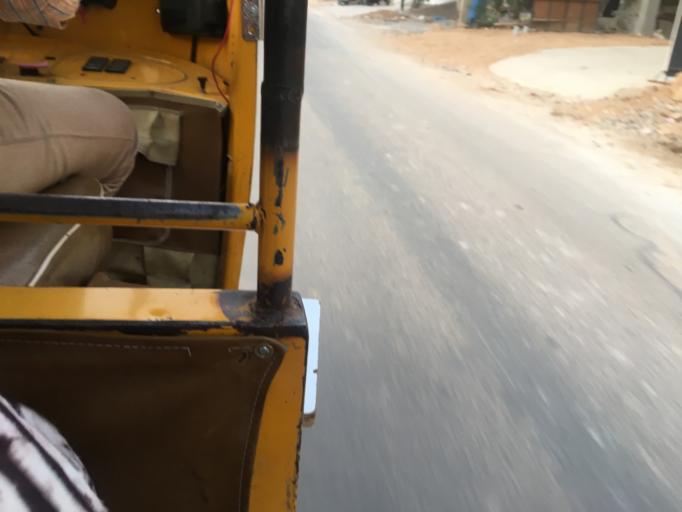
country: IN
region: Telangana
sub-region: Medak
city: Serilingampalle
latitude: 17.4302
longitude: 78.3331
